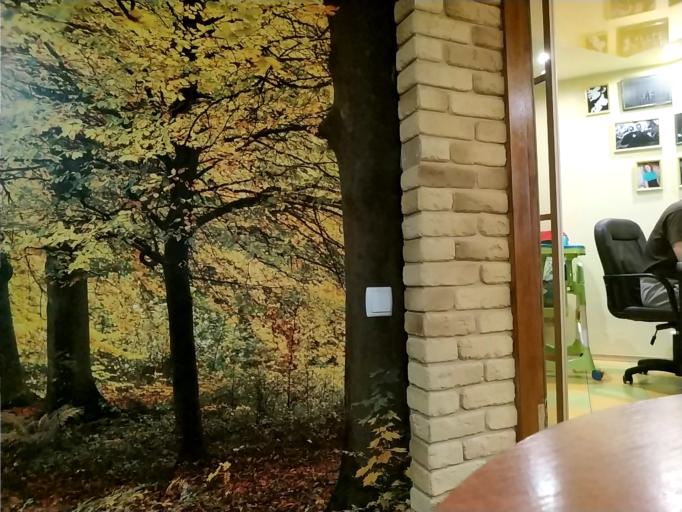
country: RU
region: Tverskaya
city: Staraya Toropa
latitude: 56.3348
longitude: 31.8736
